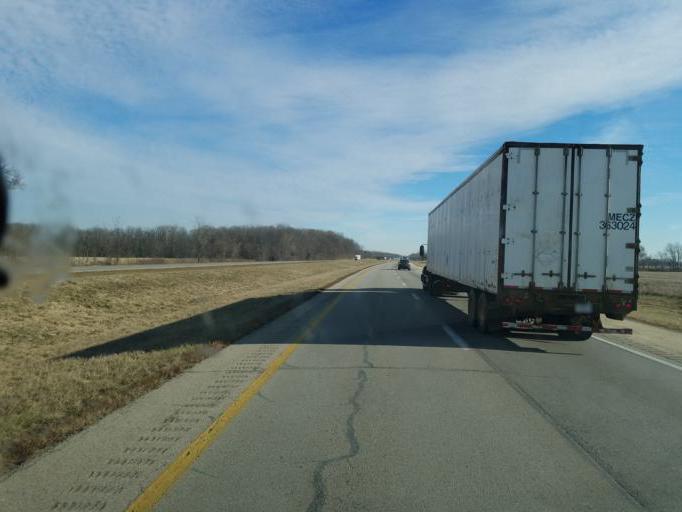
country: US
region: Ohio
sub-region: Preble County
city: New Paris
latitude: 39.8354
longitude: -84.7081
